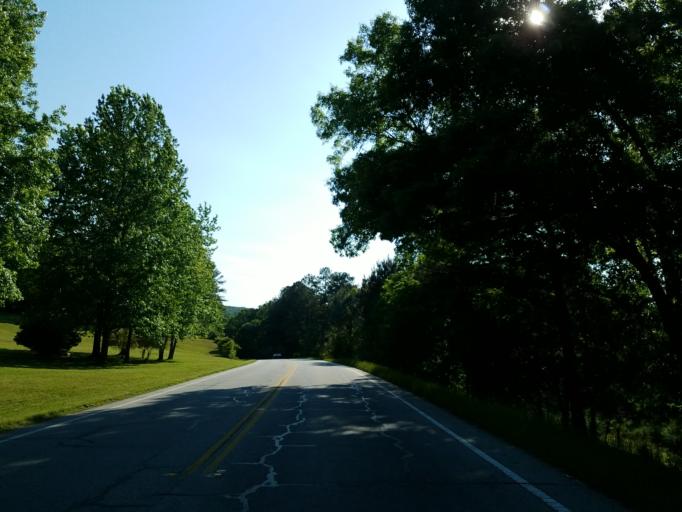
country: US
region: Georgia
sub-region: Paulding County
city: Dallas
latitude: 33.8660
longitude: -84.9022
